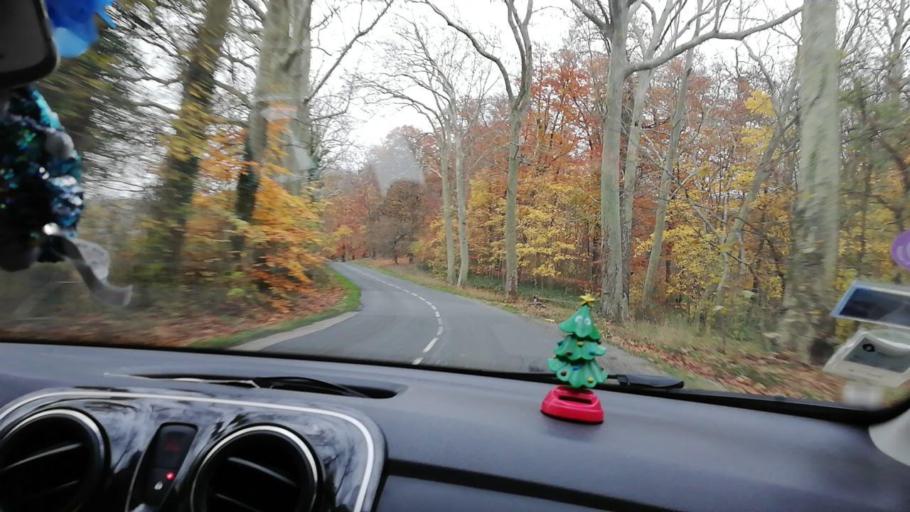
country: FR
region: Picardie
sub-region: Departement de l'Oise
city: Lagny-le-Sec
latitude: 49.0404
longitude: 2.7461
